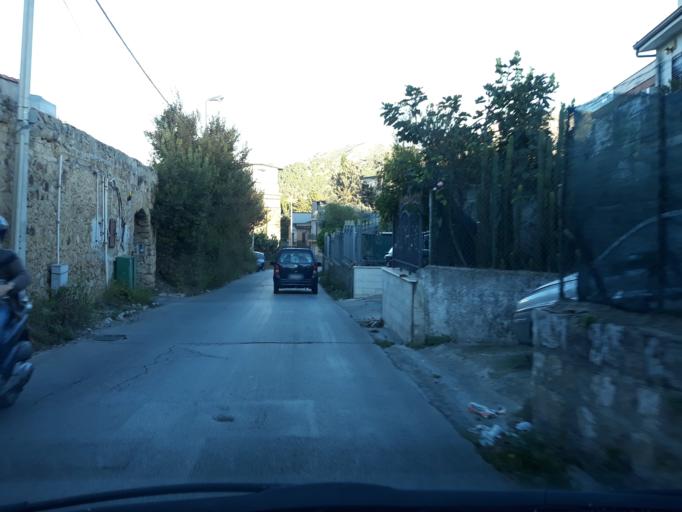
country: IT
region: Sicily
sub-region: Palermo
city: Monreale
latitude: 38.0747
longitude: 13.3066
